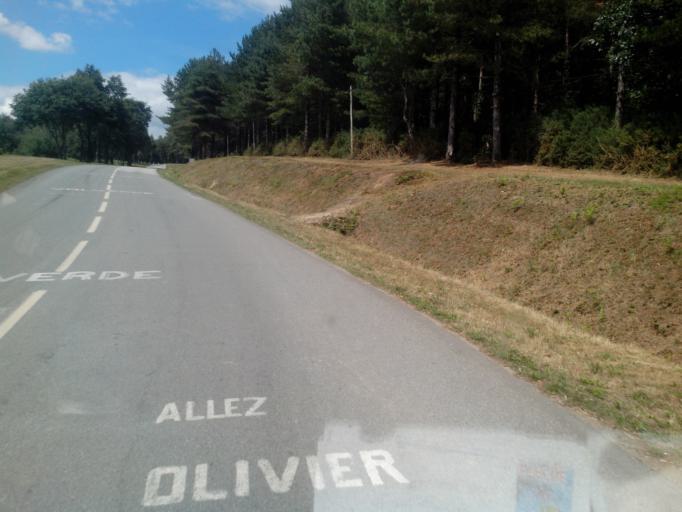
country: FR
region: Brittany
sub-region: Departement du Morbihan
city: Plumelec
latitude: 47.8304
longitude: -2.6493
